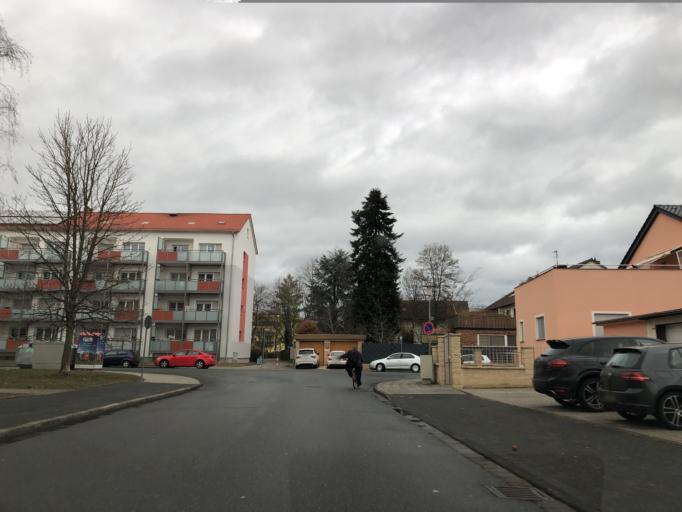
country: DE
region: Hesse
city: Raunheim
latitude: 49.9879
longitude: 8.4503
